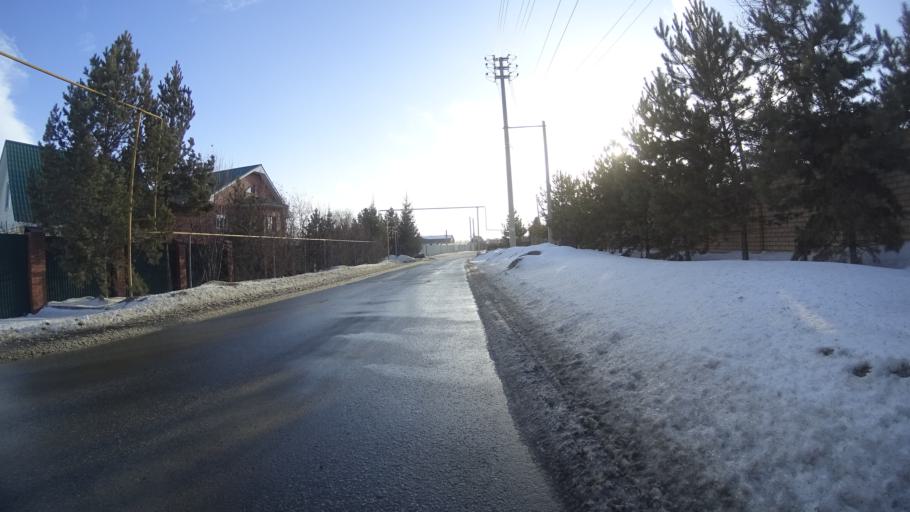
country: RU
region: Chelyabinsk
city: Sargazy
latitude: 55.1115
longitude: 61.2793
